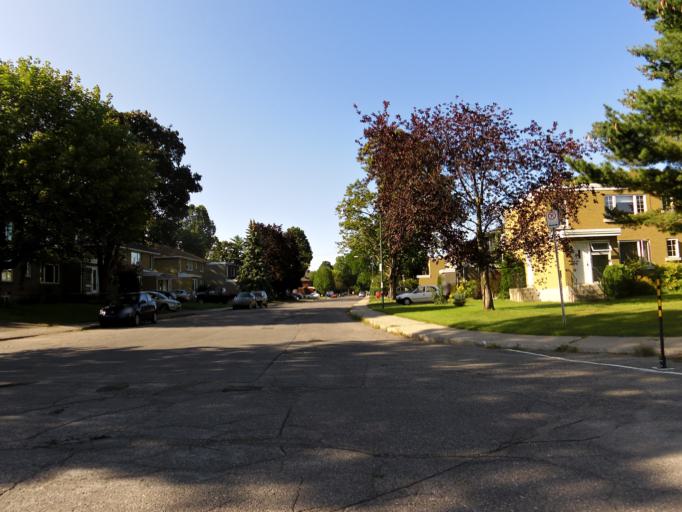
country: CA
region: Ontario
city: Ottawa
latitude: 45.4210
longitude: -75.7537
